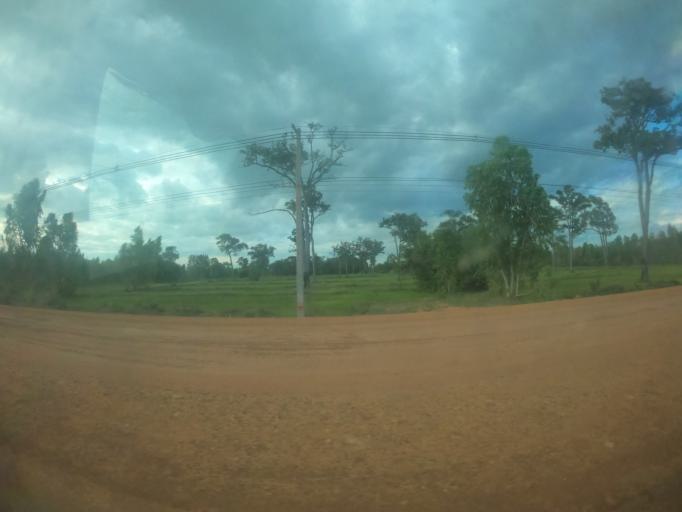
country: TH
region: Surin
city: Kap Choeng
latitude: 14.4588
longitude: 103.6666
